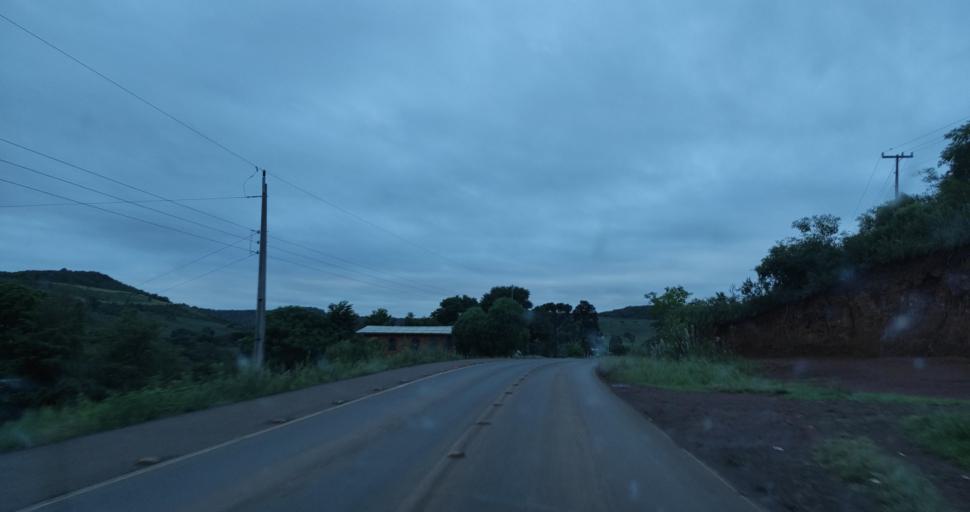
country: BR
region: Santa Catarina
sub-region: Xanxere
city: Xanxere
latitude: -26.6695
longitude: -52.4352
